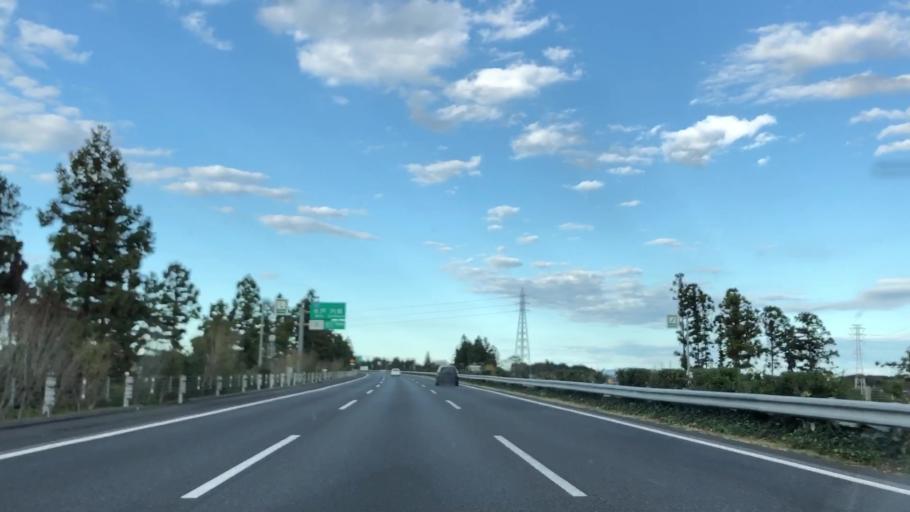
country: JP
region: Ibaraki
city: Mito-shi
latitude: 36.3717
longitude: 140.3834
